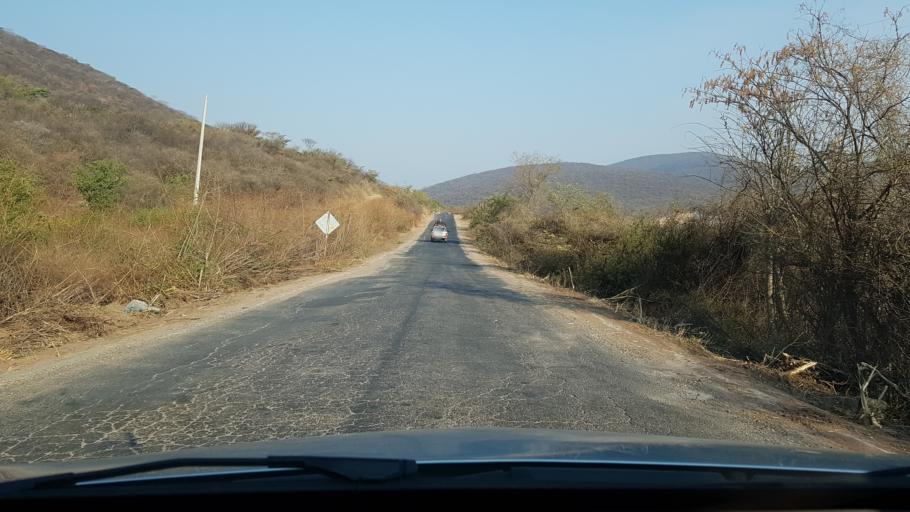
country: MX
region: Morelos
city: Tlaltizapan
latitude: 18.6709
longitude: -99.0550
